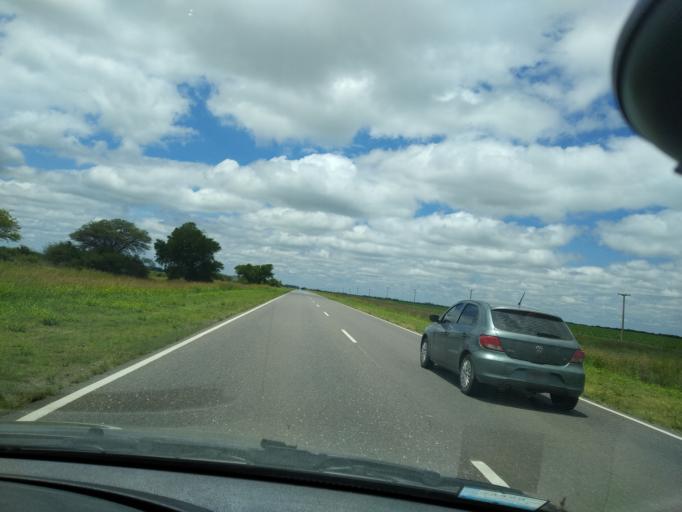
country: AR
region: Cordoba
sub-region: Departamento de Rio Segundo
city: Rio Segundo
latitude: -31.6441
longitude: -63.9850
